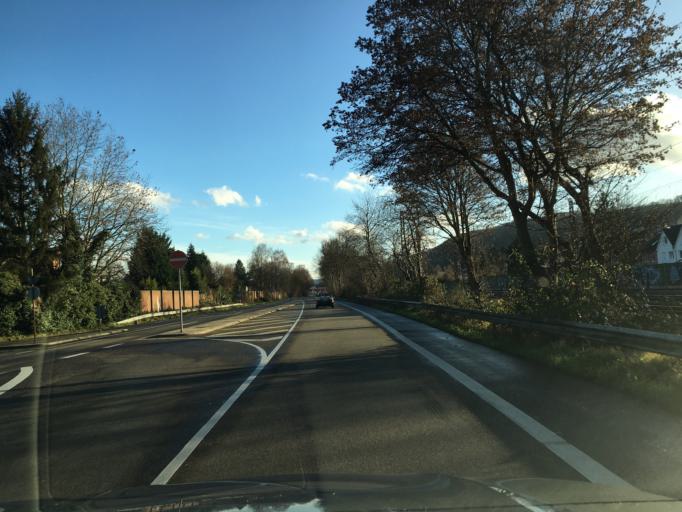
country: DE
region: North Rhine-Westphalia
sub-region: Regierungsbezirk Koln
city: Konigswinter
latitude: 50.6563
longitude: 7.1937
